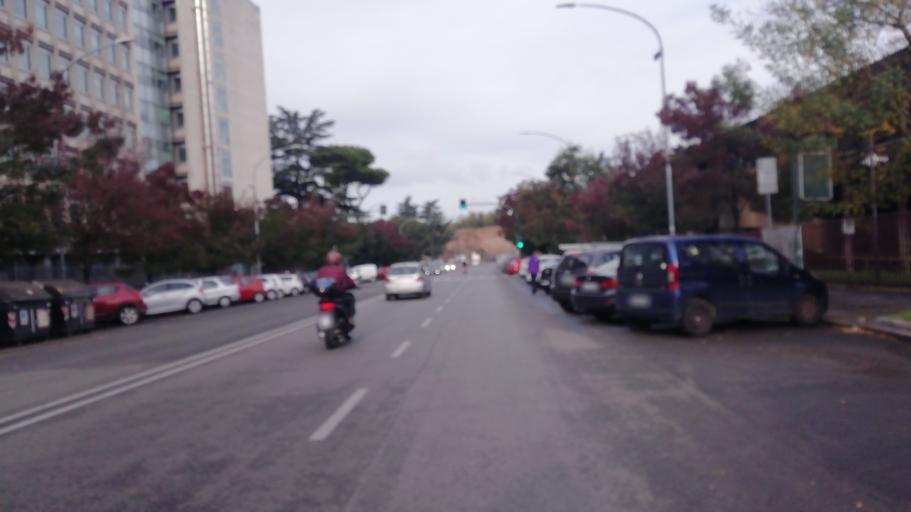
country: IT
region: Latium
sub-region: Citta metropolitana di Roma Capitale
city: Rome
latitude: 41.8753
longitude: 12.4848
